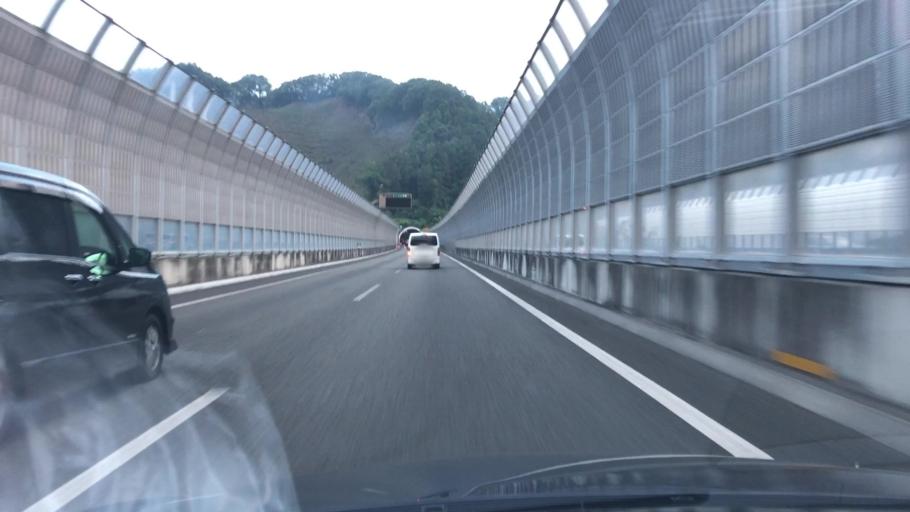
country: JP
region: Tokyo
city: Itsukaichi
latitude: 35.6673
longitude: 139.2502
